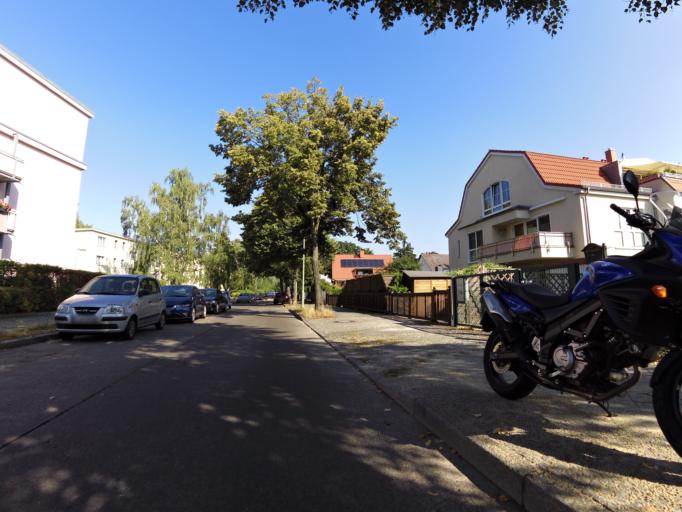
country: DE
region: Berlin
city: Lichtenrade
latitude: 52.3995
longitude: 13.3959
